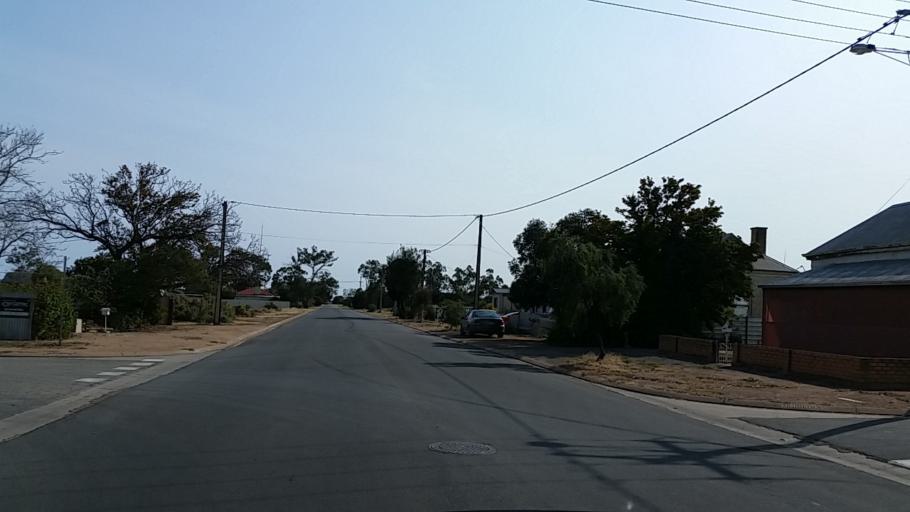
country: AU
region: South Australia
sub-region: Port Pirie City and Dists
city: Port Pirie
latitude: -33.1793
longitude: 137.9912
